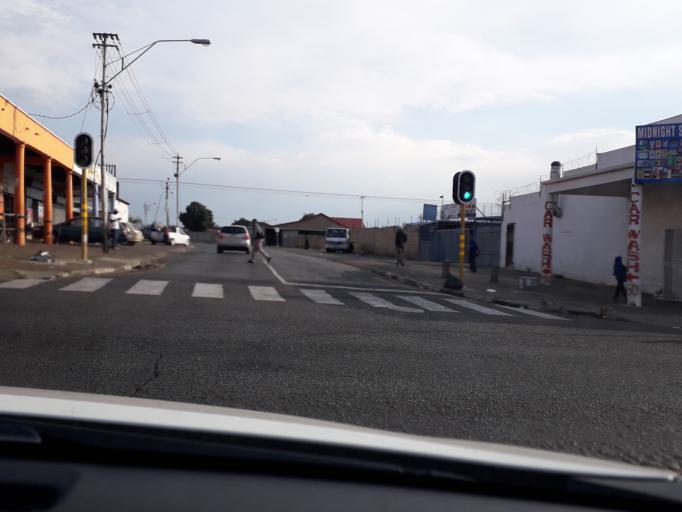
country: ZA
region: Gauteng
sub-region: City of Johannesburg Metropolitan Municipality
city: Johannesburg
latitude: -26.1757
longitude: 27.9673
